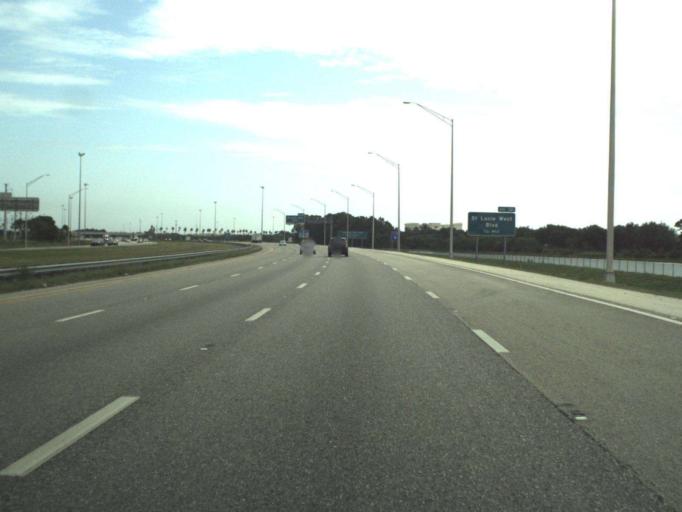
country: US
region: Florida
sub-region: Saint Lucie County
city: Port Saint Lucie
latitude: 27.2991
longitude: -80.4150
